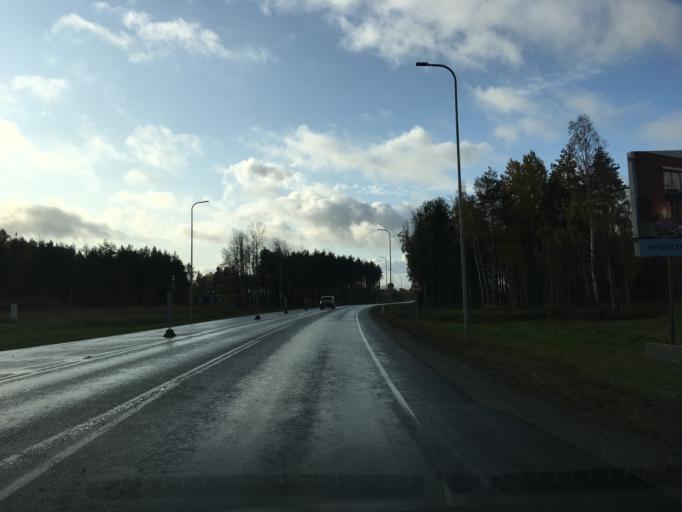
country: EE
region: Harju
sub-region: Saue vald
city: Laagri
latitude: 59.3578
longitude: 24.6004
